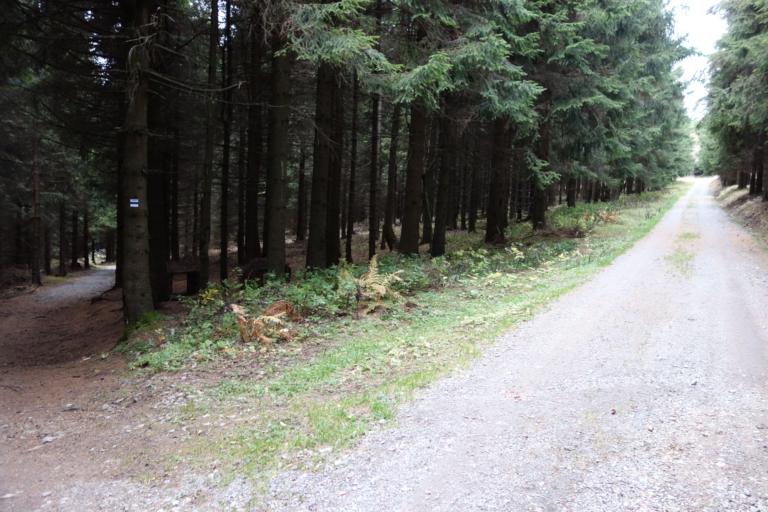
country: DE
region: Saxony
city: Kurort Oberwiesenthal
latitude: 50.4399
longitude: 12.9755
